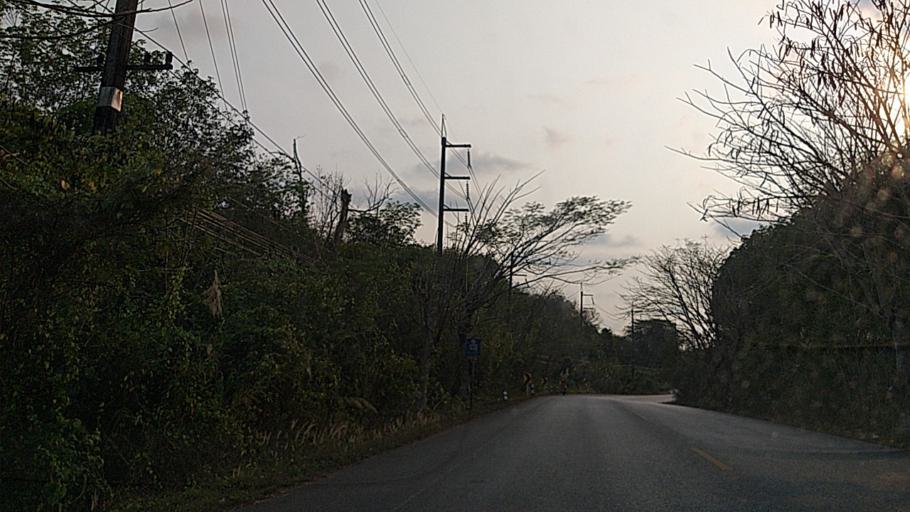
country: TH
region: Trat
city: Khao Saming
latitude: 12.2987
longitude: 102.3391
